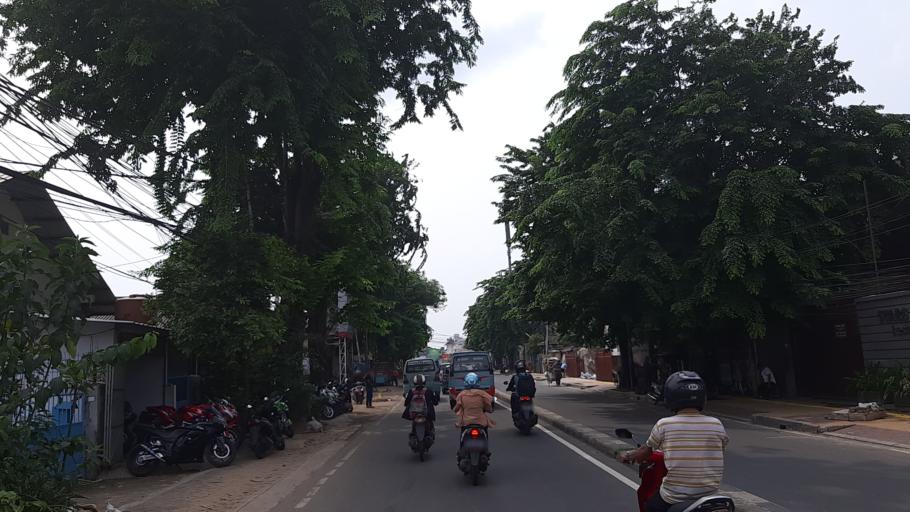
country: ID
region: Jakarta Raya
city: Jakarta
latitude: -6.2068
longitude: 106.7851
